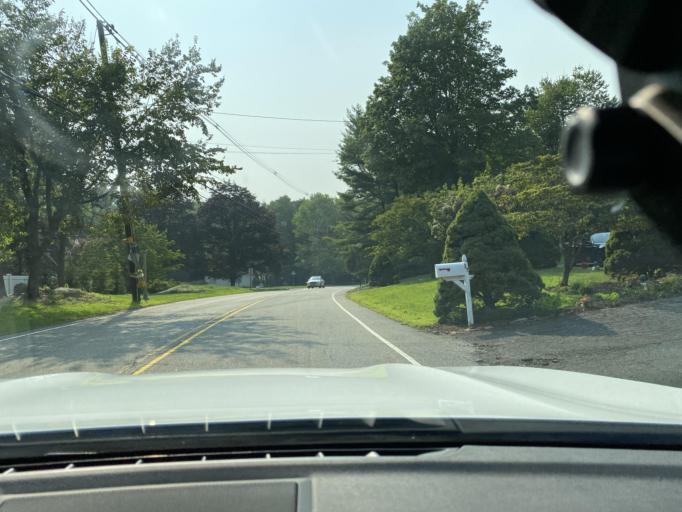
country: US
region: New York
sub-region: Rockland County
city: Airmont
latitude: 41.0814
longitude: -74.1210
